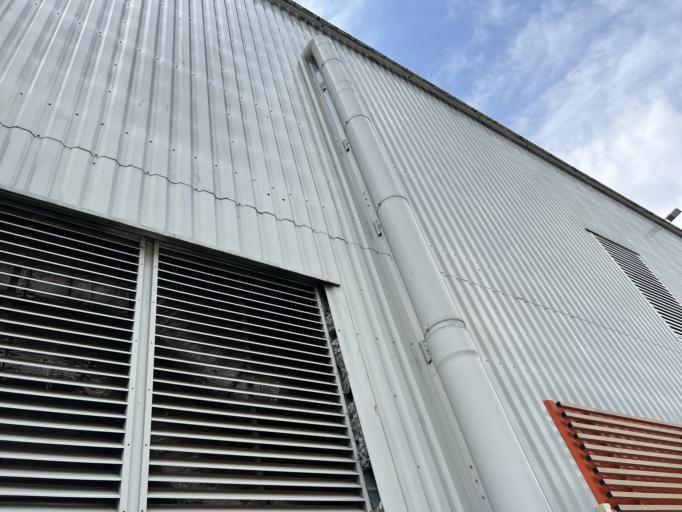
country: FR
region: Provence-Alpes-Cote d'Azur
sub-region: Departement des Alpes-Maritimes
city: Gattieres
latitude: 43.7269
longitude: 7.1902
